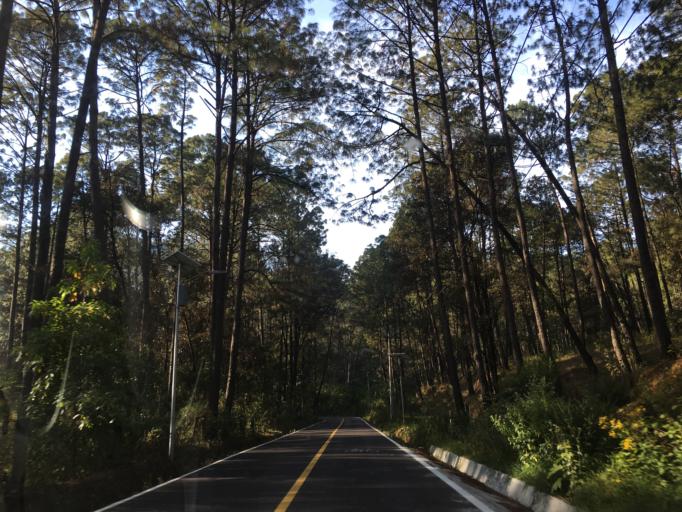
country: MX
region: Mexico
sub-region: Valle de Bravo
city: Casas Viejas
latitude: 19.1474
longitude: -100.1209
